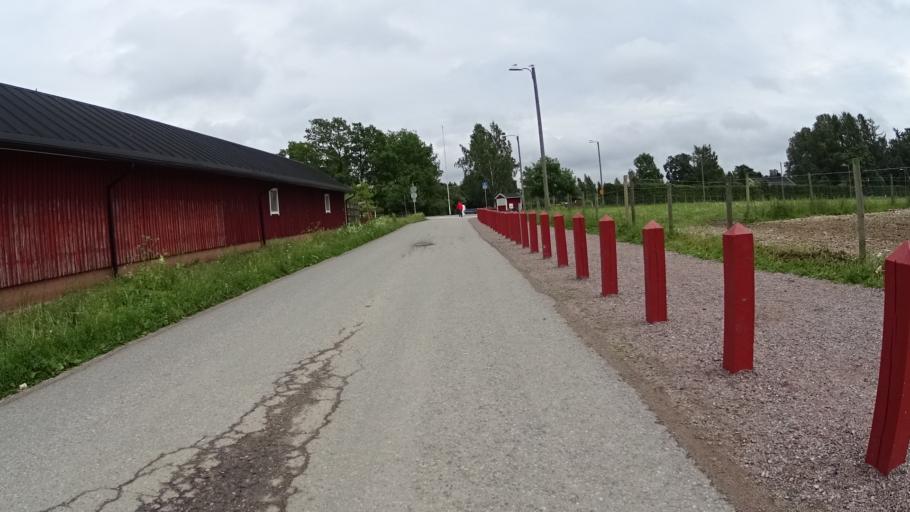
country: FI
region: Uusimaa
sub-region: Helsinki
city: Vantaa
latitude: 60.2753
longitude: 24.9527
